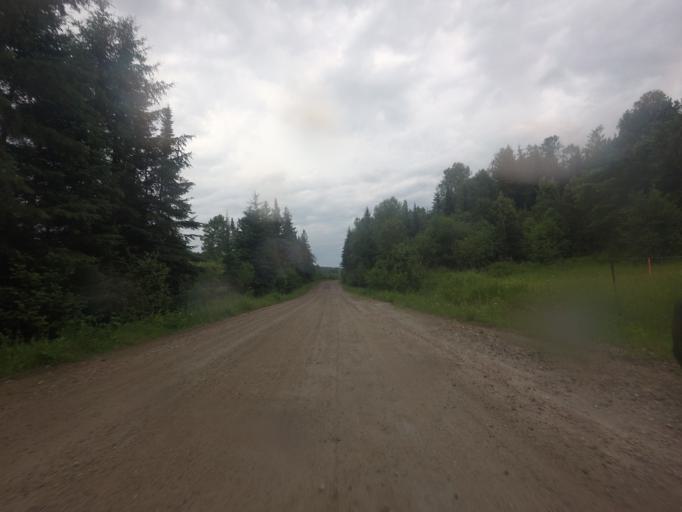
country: CA
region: Quebec
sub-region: Outaouais
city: Maniwaki
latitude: 46.4465
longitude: -75.9353
